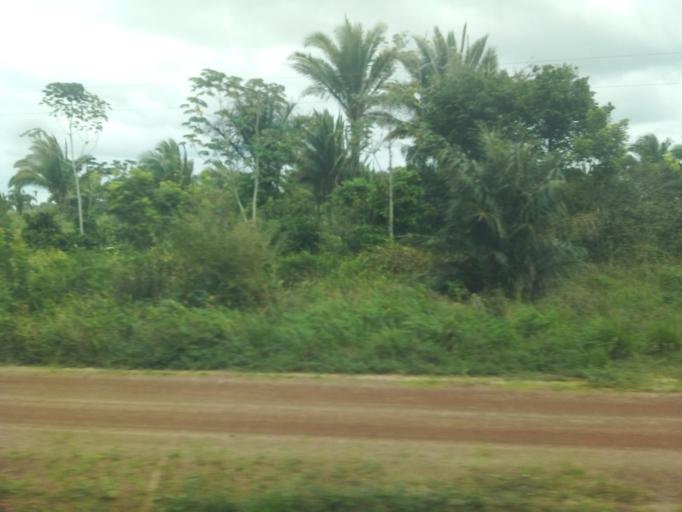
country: BR
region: Maranhao
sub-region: Itapecuru Mirim
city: Itapecuru Mirim
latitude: -3.2161
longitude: -44.4028
